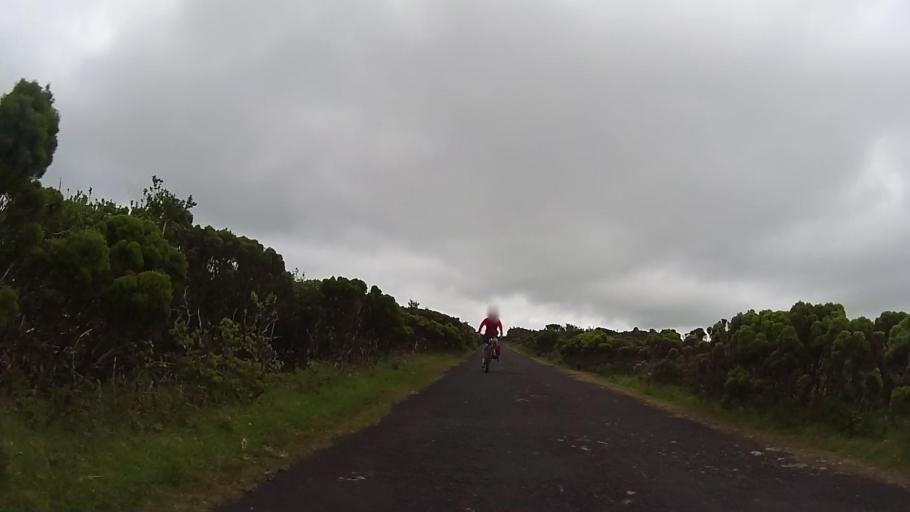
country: PT
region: Azores
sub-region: Sao Roque do Pico
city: Sao Roque do Pico
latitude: 38.4649
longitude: -28.2879
